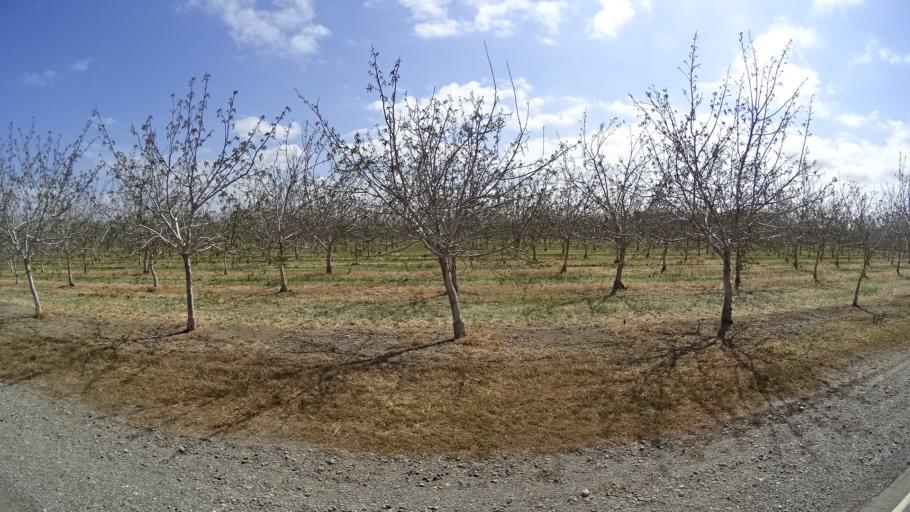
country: US
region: California
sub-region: Butte County
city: Biggs
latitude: 39.4284
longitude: -121.9296
